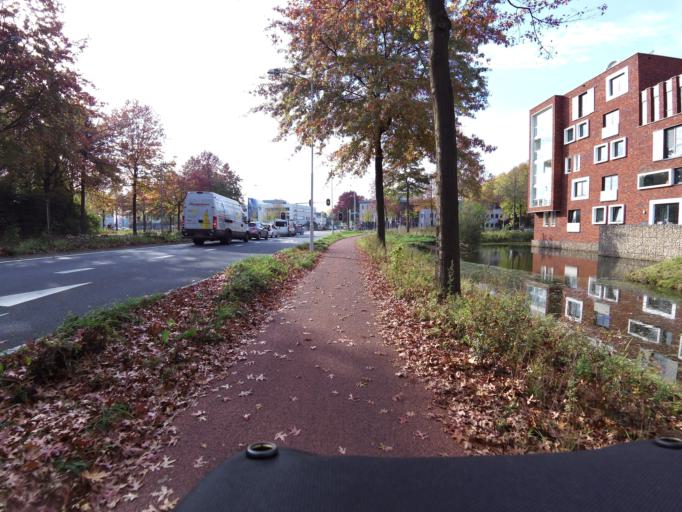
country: NL
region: Gelderland
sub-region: Gemeente Wageningen
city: Wageningen
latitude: 51.9779
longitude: 5.6499
